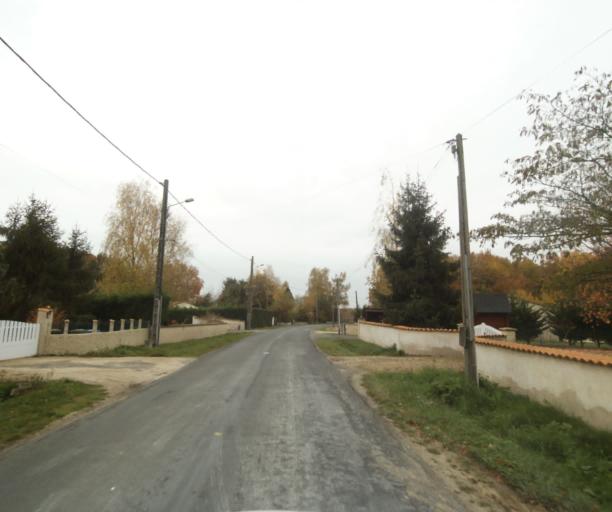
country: FR
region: Poitou-Charentes
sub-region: Departement de la Charente-Maritime
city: Chermignac
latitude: 45.7165
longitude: -0.6935
